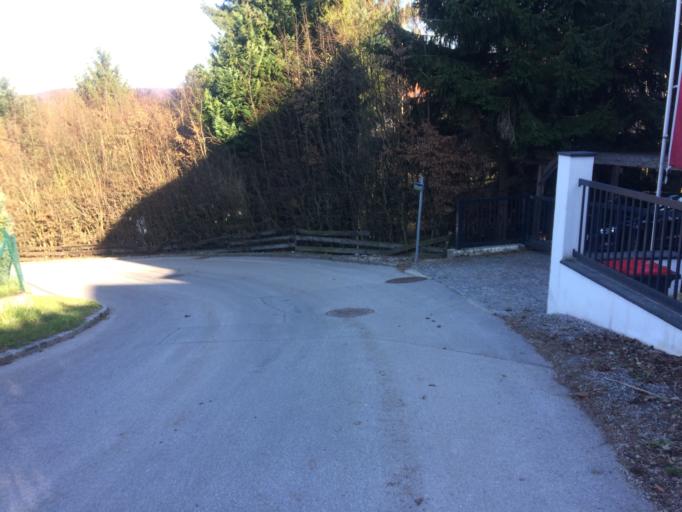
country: AT
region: Lower Austria
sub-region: Politischer Bezirk Wien-Umgebung
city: Gablitz
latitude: 48.2208
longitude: 16.1339
